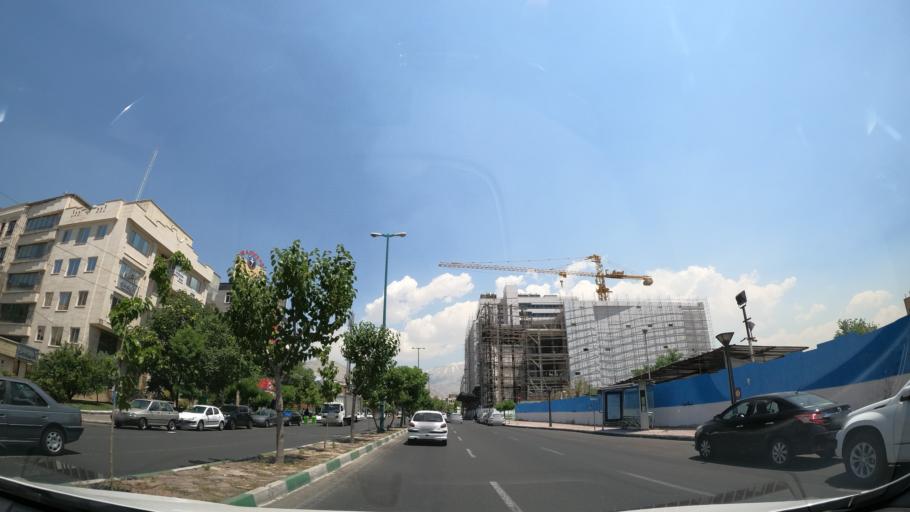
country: IR
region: Tehran
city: Tajrish
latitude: 35.7690
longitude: 51.3788
